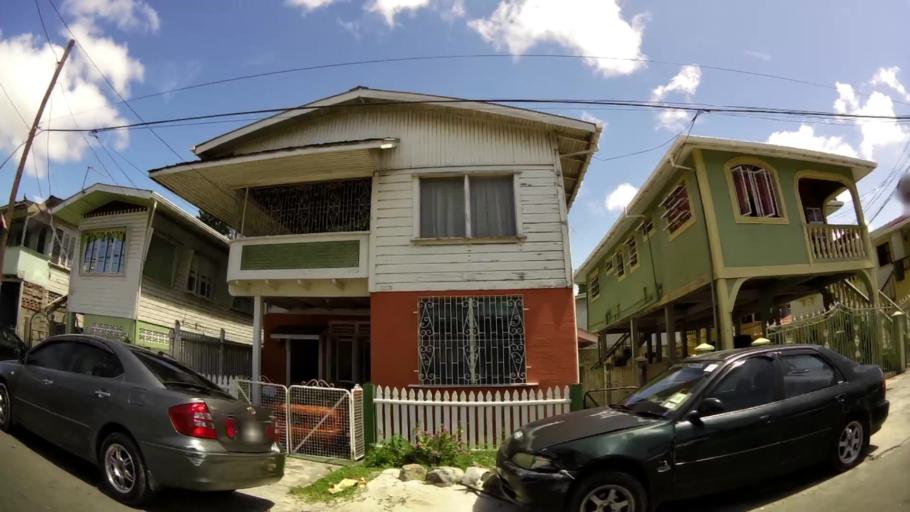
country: GY
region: Demerara-Mahaica
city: Georgetown
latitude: 6.8043
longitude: -58.1615
